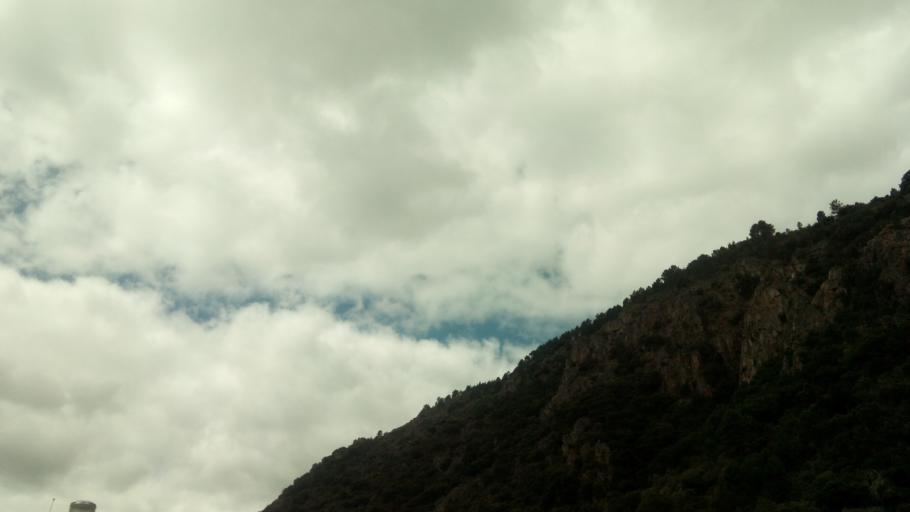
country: ES
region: Galicia
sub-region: Provincia de Lugo
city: Lobios
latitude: 42.4050
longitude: -7.5766
